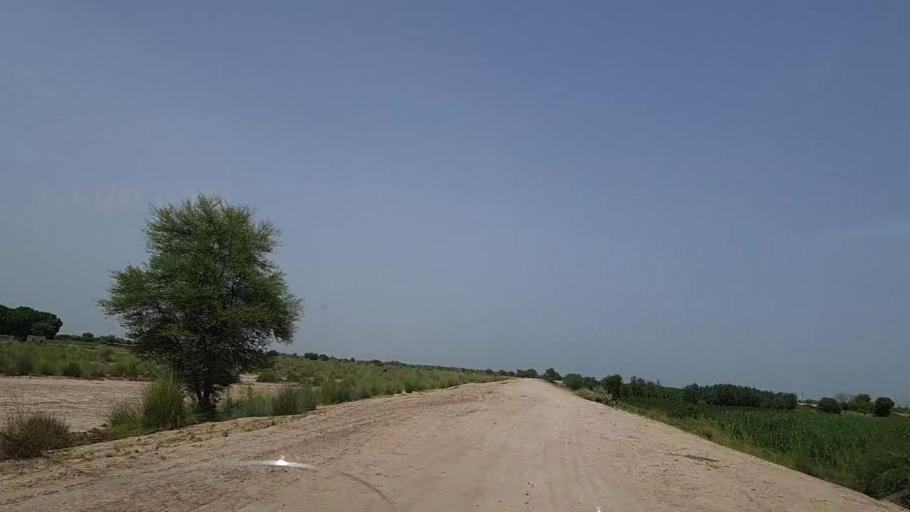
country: PK
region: Sindh
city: Kandiaro
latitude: 27.0548
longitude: 68.1241
